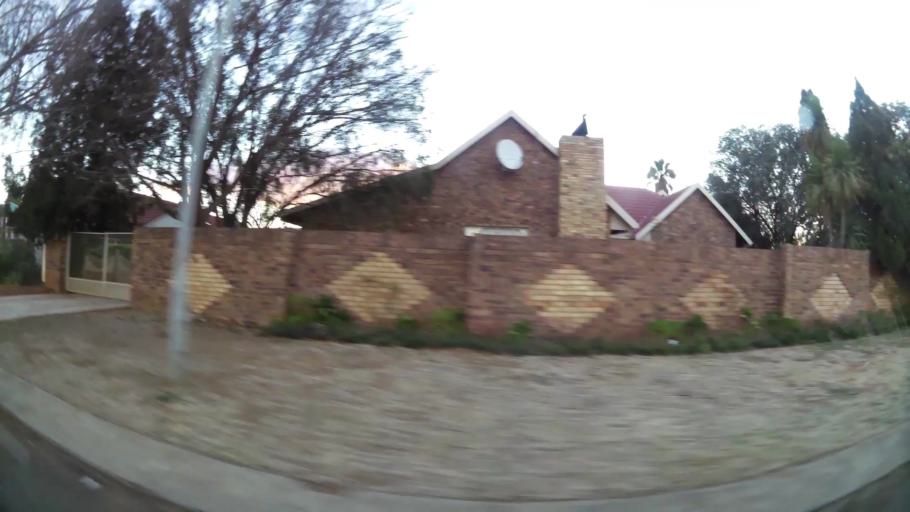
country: ZA
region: North-West
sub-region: Dr Kenneth Kaunda District Municipality
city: Potchefstroom
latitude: -26.7182
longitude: 27.1233
